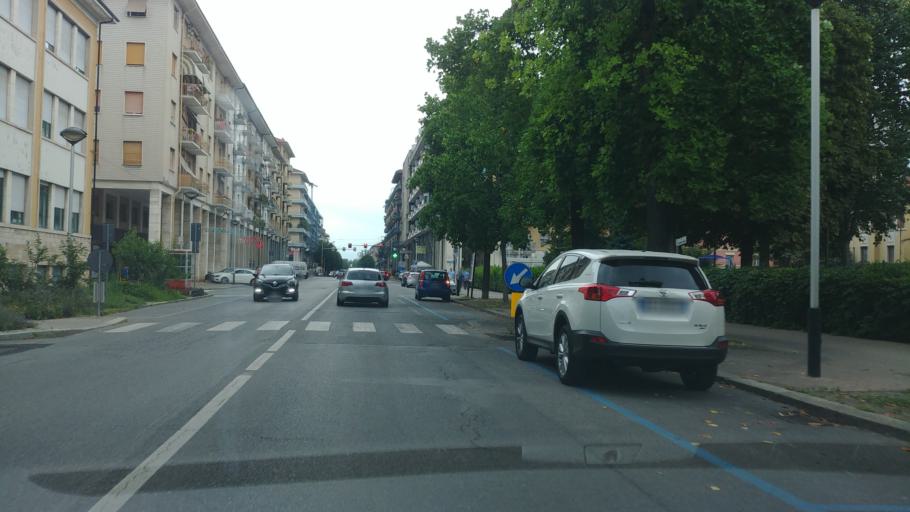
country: IT
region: Piedmont
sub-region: Provincia di Cuneo
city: Cuneo
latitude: 44.3823
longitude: 7.5375
